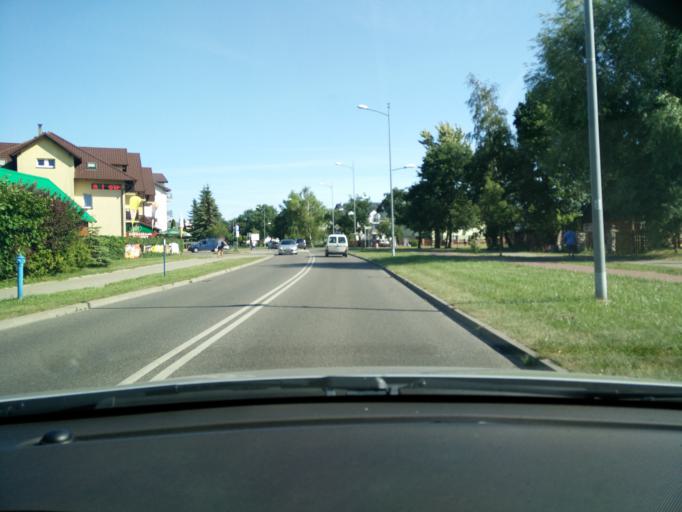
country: PL
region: Pomeranian Voivodeship
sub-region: Powiat pucki
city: Jastarnia
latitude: 54.7046
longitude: 18.6598
